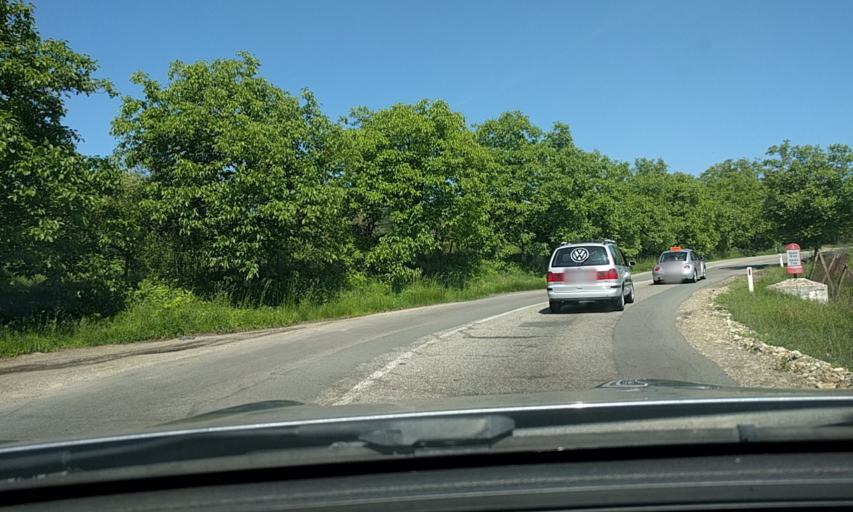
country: RO
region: Bistrita-Nasaud
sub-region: Municipiul Bistrita
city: Unirea
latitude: 47.1701
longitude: 24.4966
